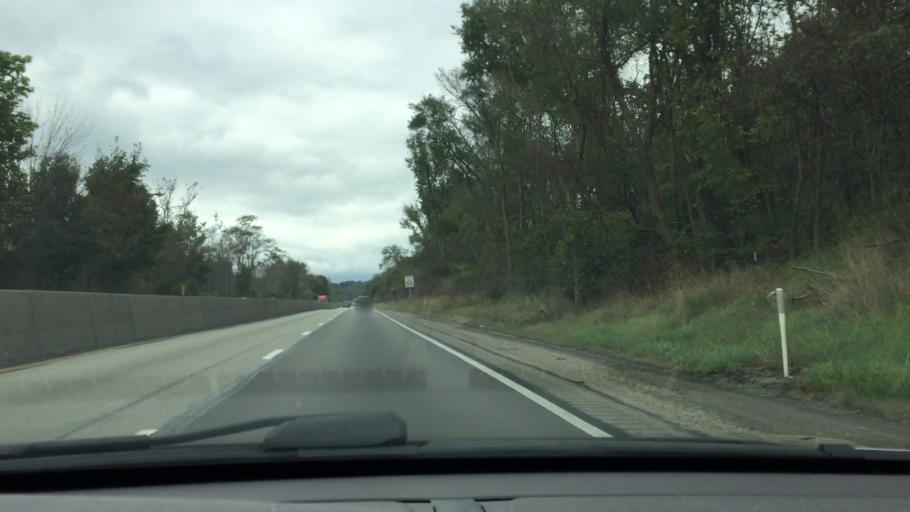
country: US
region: Pennsylvania
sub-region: Westmoreland County
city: Fellsburg
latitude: 40.1535
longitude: -79.7828
